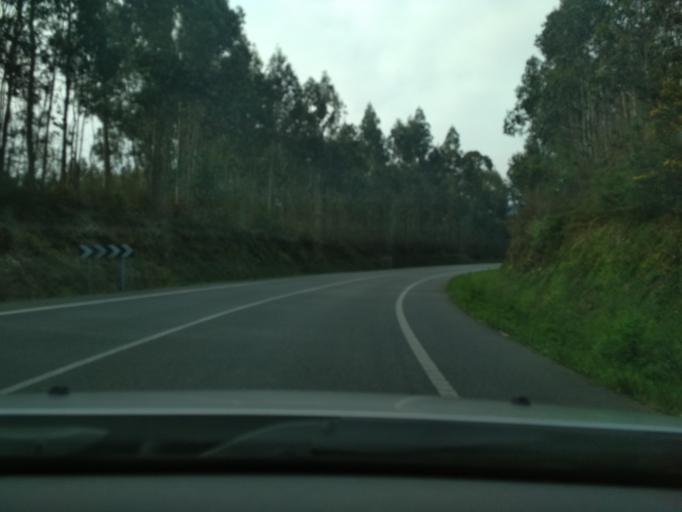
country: ES
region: Galicia
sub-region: Provincia de Pontevedra
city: Catoira
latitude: 42.6614
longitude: -8.7022
